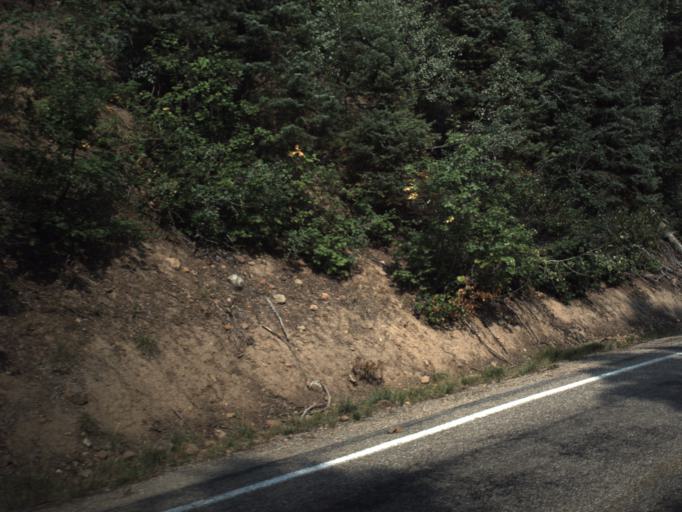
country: US
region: Utah
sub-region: Summit County
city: Summit Park
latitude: 40.8383
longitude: -111.6410
